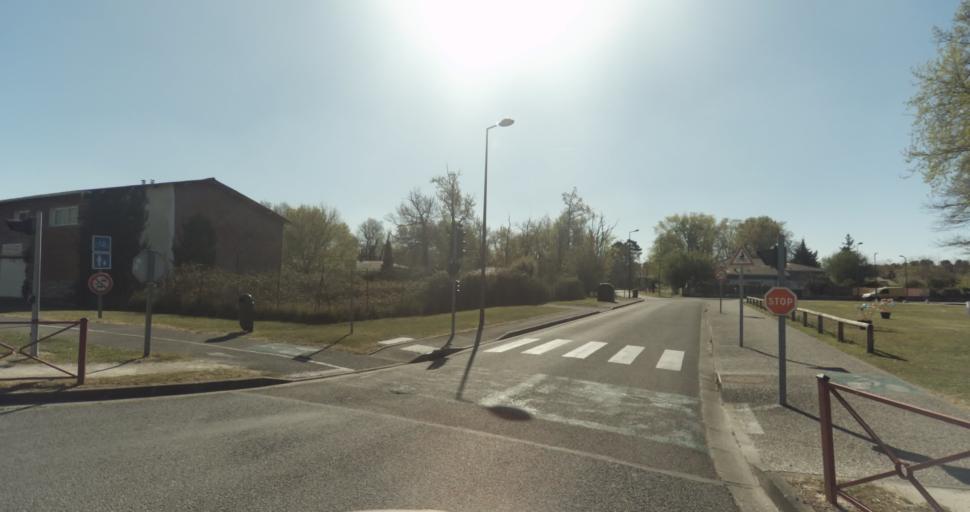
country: FR
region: Aquitaine
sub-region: Departement de la Gironde
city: Martignas-sur-Jalle
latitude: 44.7985
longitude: -0.8367
